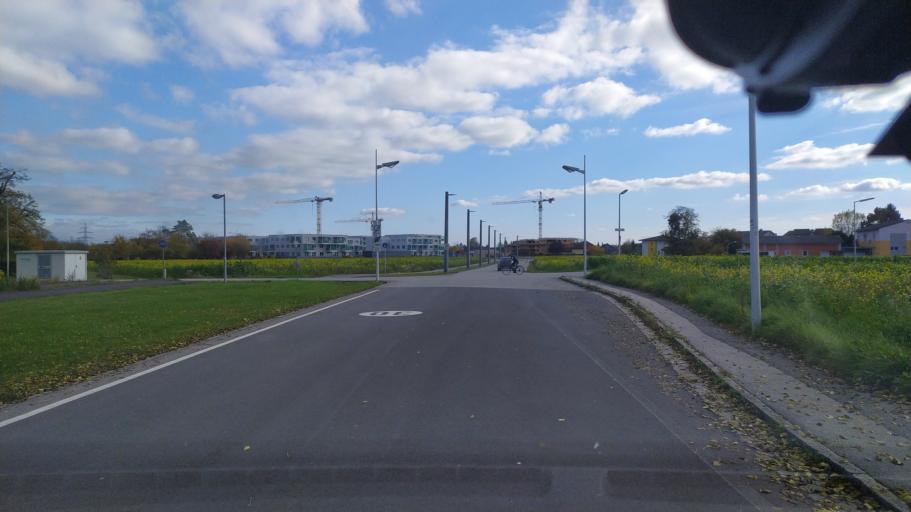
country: AT
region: Upper Austria
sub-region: Politischer Bezirk Urfahr-Umgebung
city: Steyregg
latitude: 48.2564
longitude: 14.3639
